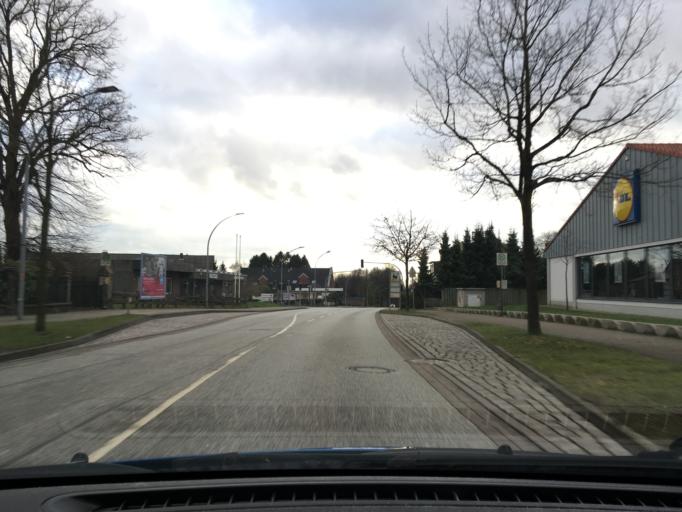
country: DE
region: Schleswig-Holstein
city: Ottenbuttel
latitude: 53.9512
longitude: 9.4944
